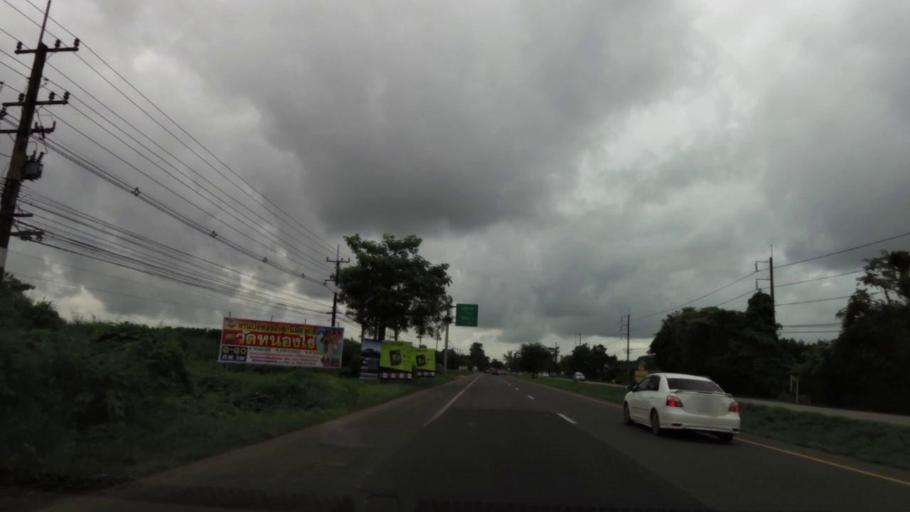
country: TH
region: Chanthaburi
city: Tha Mai
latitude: 12.6650
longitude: 102.0080
